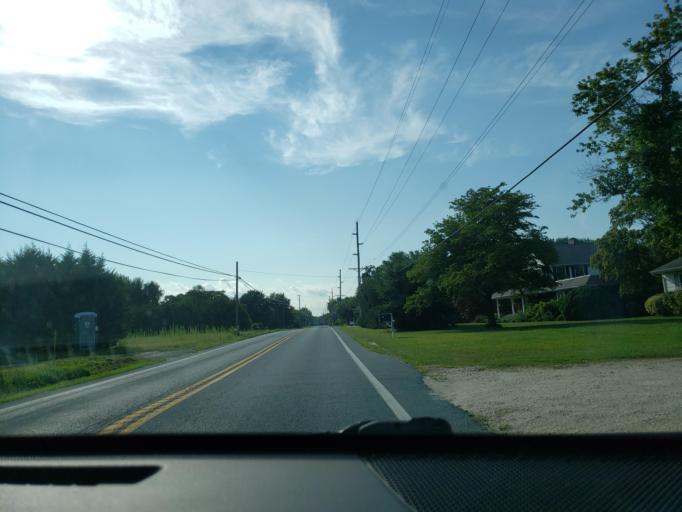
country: US
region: Delaware
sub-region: Sussex County
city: Milton
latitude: 38.7674
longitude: -75.2869
